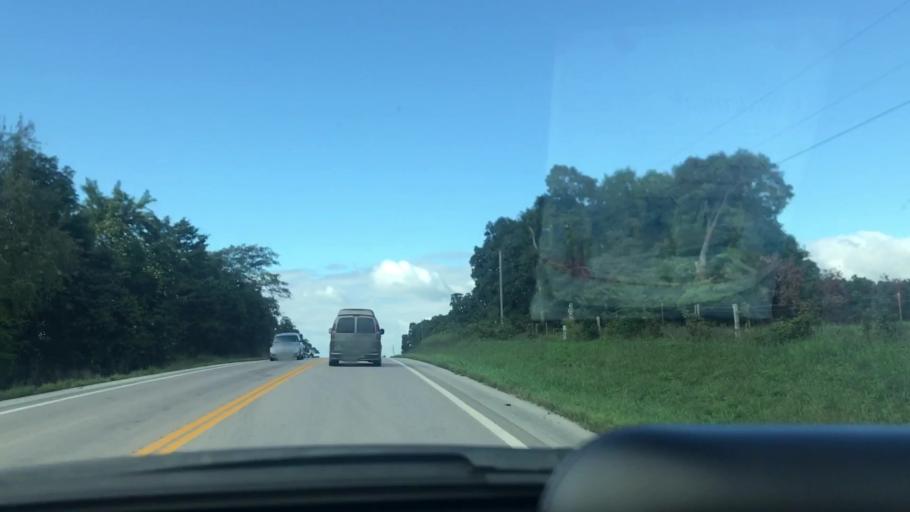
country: US
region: Missouri
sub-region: Hickory County
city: Hermitage
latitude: 37.9629
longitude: -93.2068
